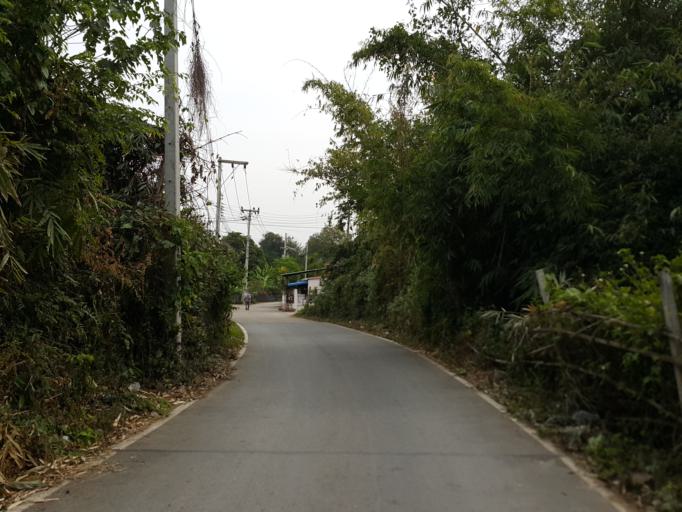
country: TH
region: Chiang Mai
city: Saraphi
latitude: 18.7418
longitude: 99.0166
